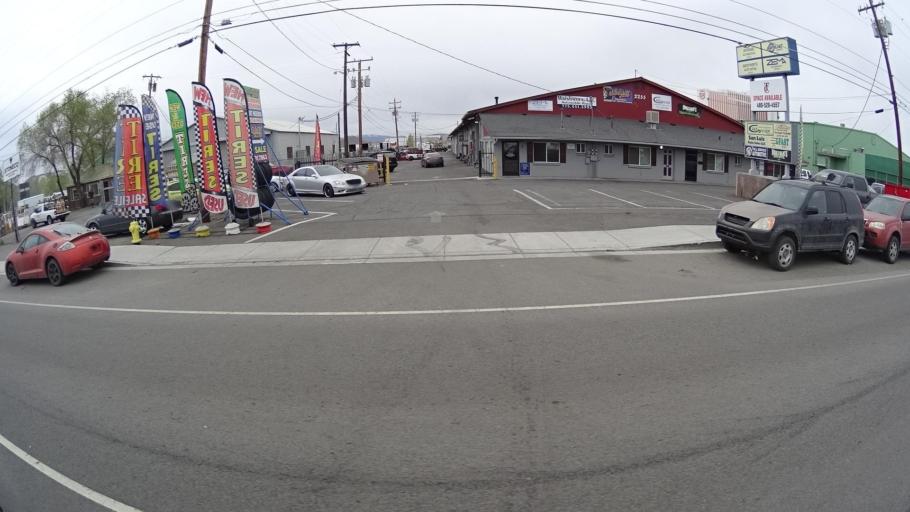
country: US
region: Nevada
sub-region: Washoe County
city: Sparks
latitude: 39.5276
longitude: -119.7744
